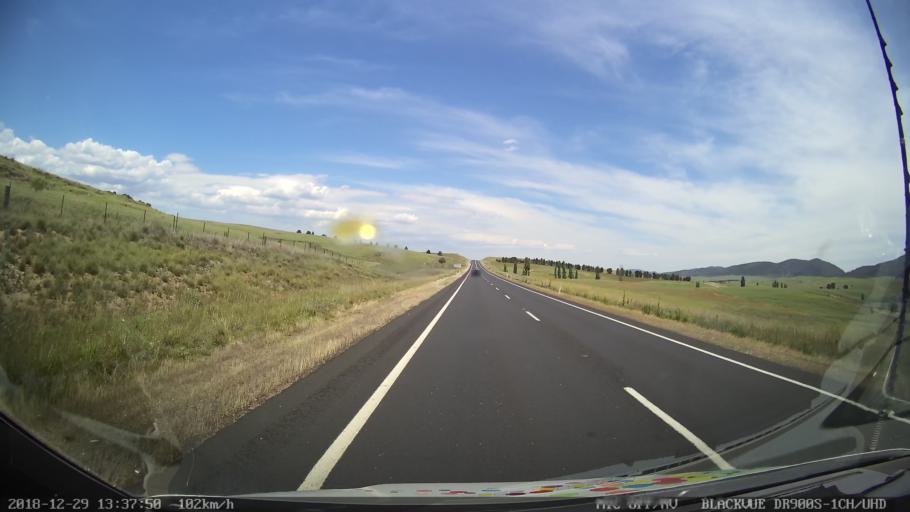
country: AU
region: New South Wales
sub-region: Cooma-Monaro
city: Cooma
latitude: -35.9899
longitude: 149.1384
